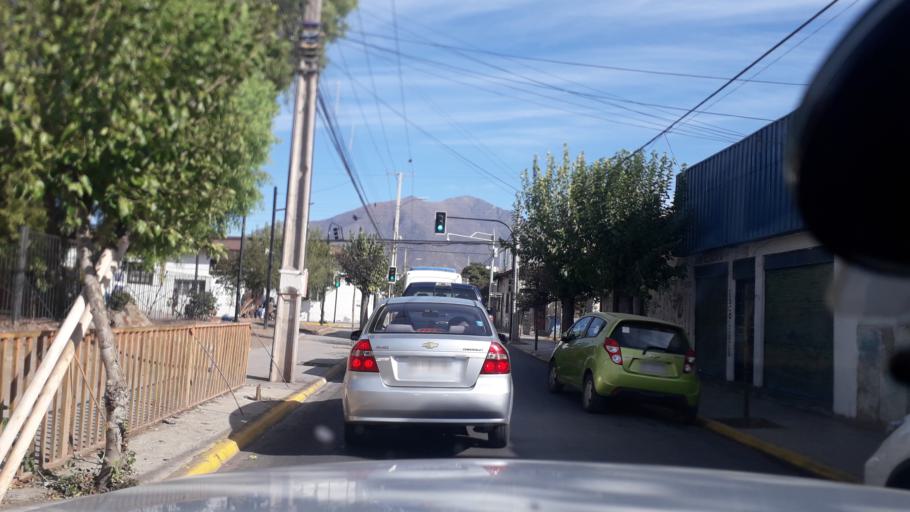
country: CL
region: Valparaiso
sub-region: Provincia de San Felipe
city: San Felipe
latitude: -32.7481
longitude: -70.7263
